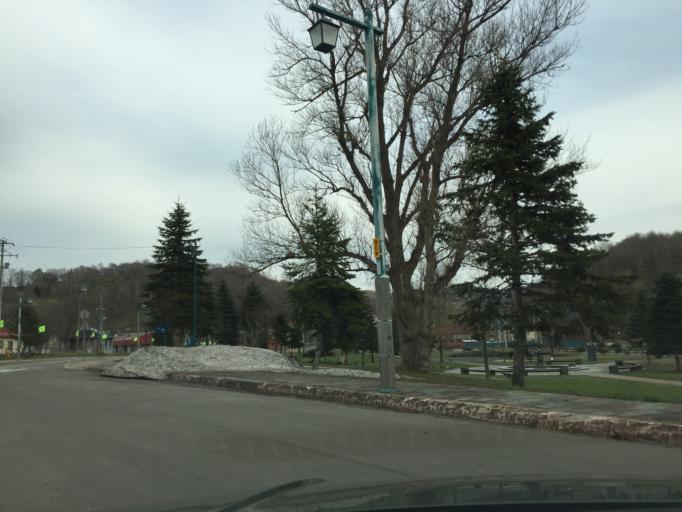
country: JP
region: Hokkaido
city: Utashinai
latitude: 43.5210
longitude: 142.0430
